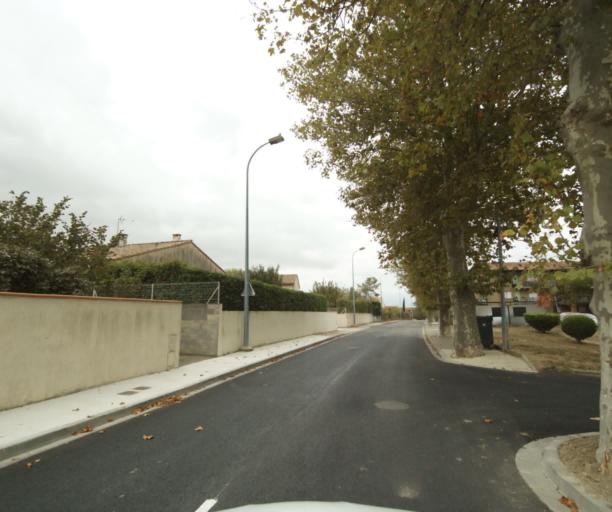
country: FR
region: Midi-Pyrenees
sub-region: Departement de la Haute-Garonne
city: Villefranche-de-Lauragais
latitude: 43.3975
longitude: 1.7266
